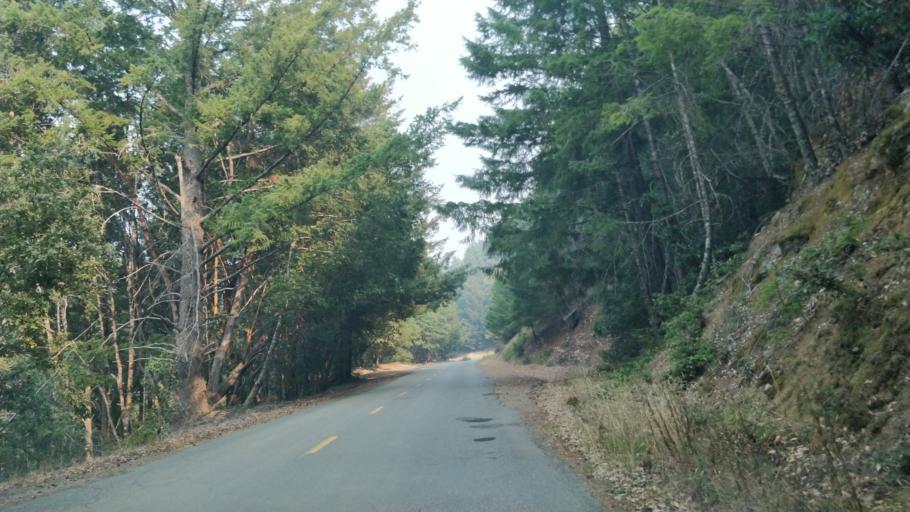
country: US
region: California
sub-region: Humboldt County
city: Rio Dell
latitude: 40.2615
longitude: -124.1002
